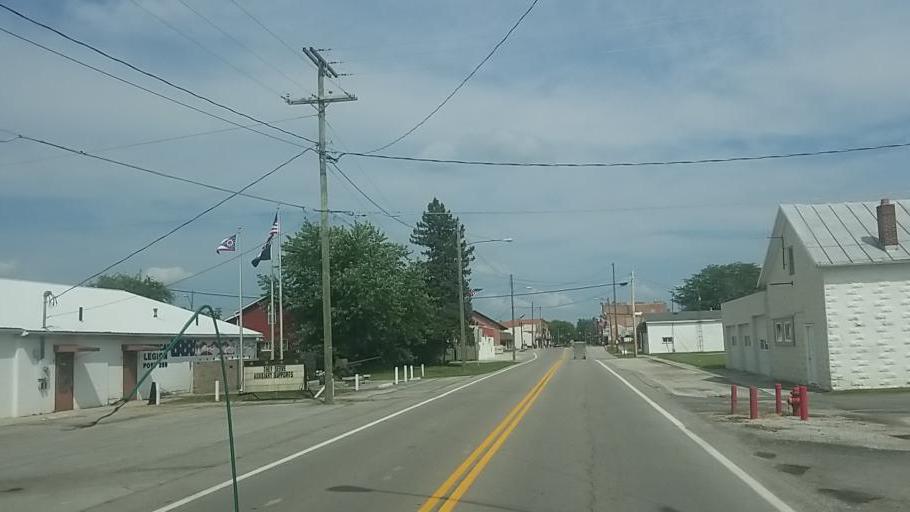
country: US
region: Ohio
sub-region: Hardin County
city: Forest
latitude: 40.8018
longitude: -83.5143
